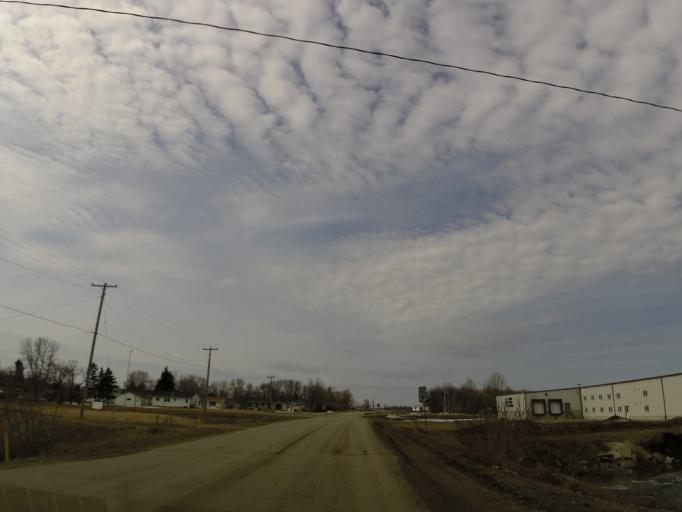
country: US
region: North Dakota
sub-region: Walsh County
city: Grafton
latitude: 48.2959
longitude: -97.3708
